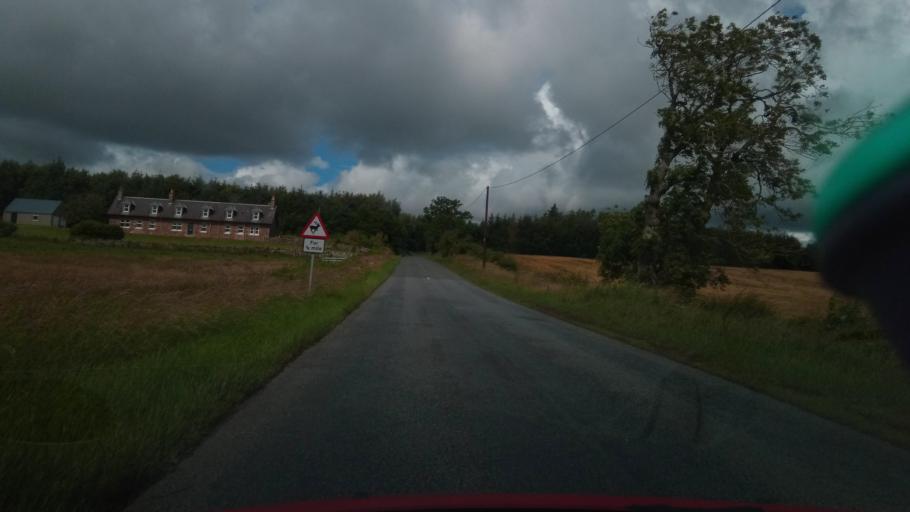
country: GB
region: Scotland
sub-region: The Scottish Borders
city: Kelso
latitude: 55.5508
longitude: -2.3961
